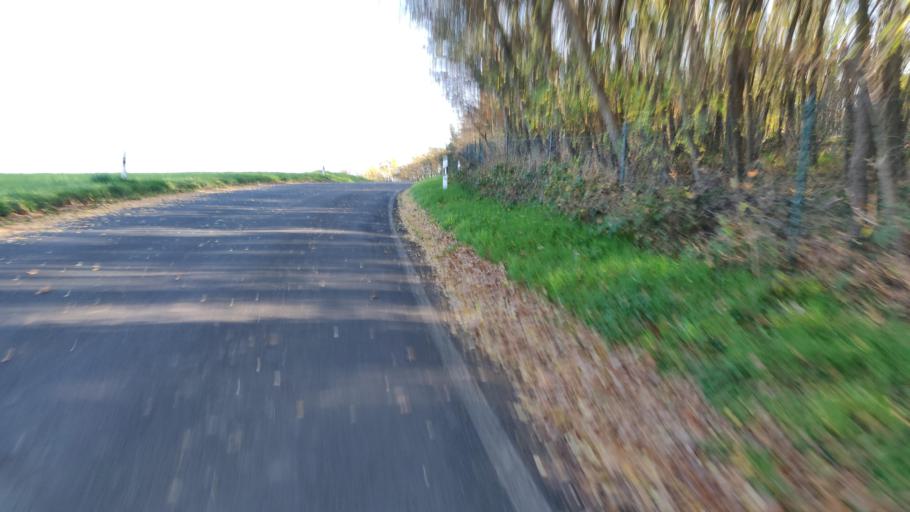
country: DE
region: Brandenburg
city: Ortrand
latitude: 51.3622
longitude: 13.7669
